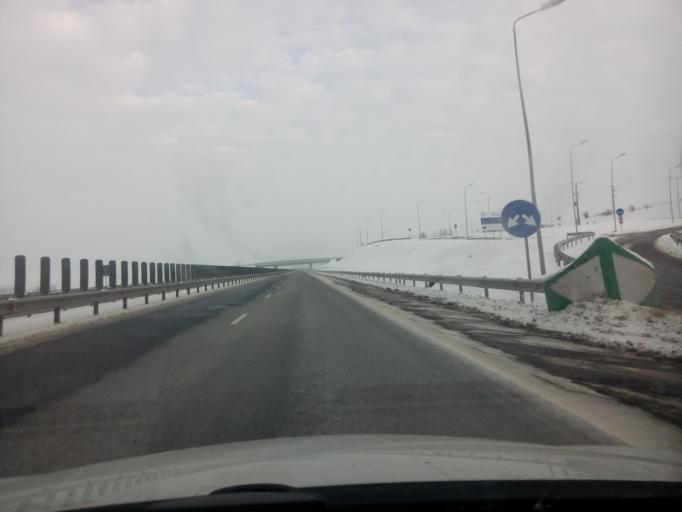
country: RO
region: Alba
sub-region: Comuna Cut
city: Cut
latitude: 45.9215
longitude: 23.6519
